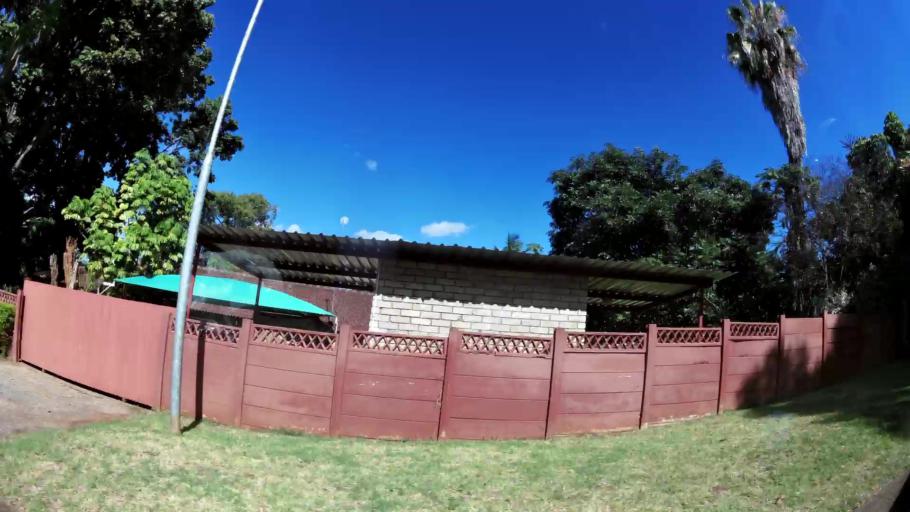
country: ZA
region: Limpopo
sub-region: Mopani District Municipality
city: Tzaneen
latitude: -23.8117
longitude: 30.1574
